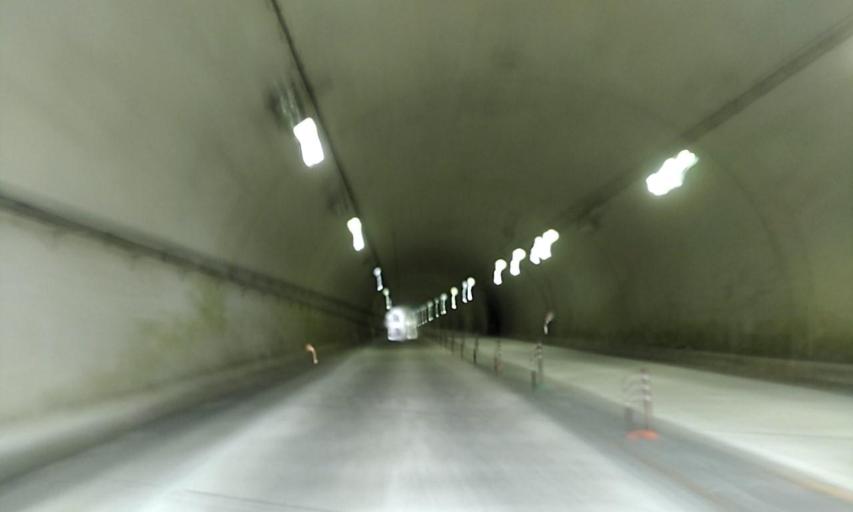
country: JP
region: Wakayama
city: Shingu
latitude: 33.6294
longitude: 135.9225
